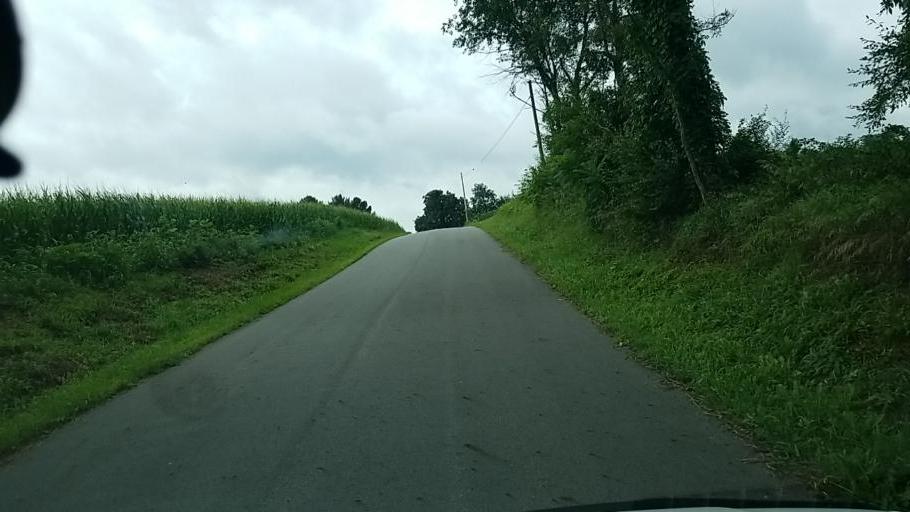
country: US
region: Pennsylvania
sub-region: Dauphin County
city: Millersburg
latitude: 40.5161
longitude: -76.8847
